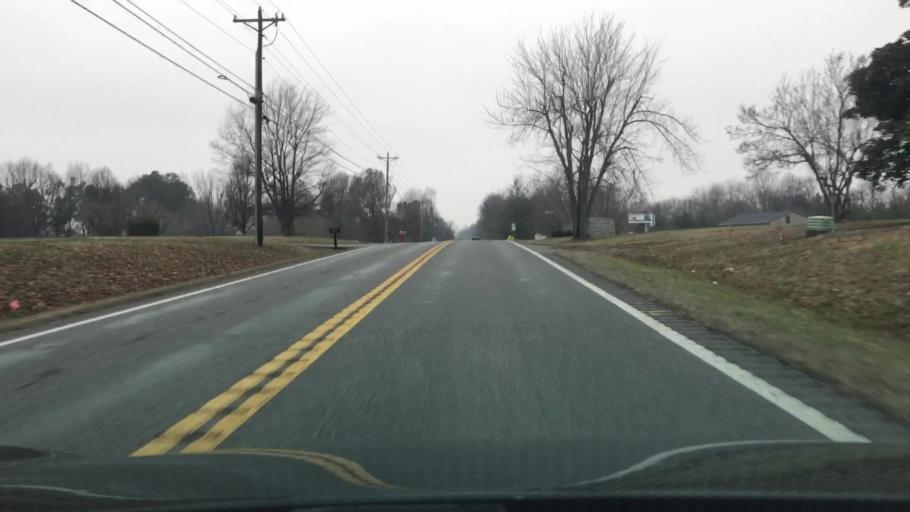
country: US
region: Kentucky
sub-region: Livingston County
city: Ledbetter
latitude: 36.9710
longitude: -88.4631
